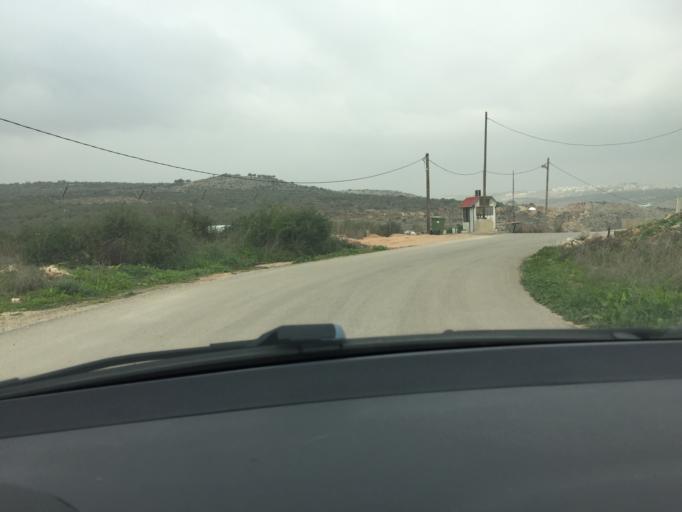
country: PS
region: West Bank
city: Al Lubban al Gharbi
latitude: 32.0441
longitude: 35.0443
